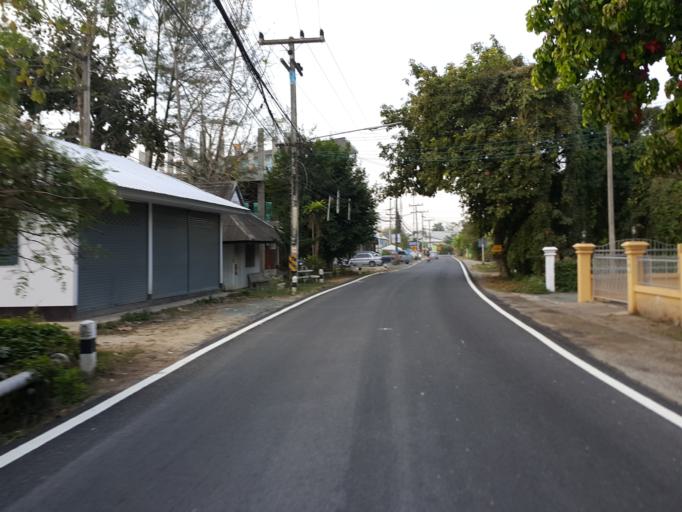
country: TH
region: Chiang Mai
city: San Sai
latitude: 18.8080
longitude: 99.0683
